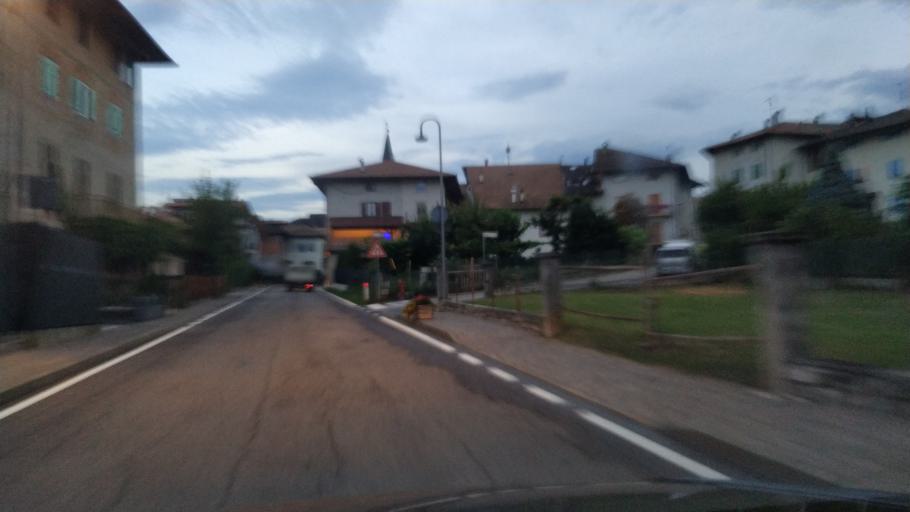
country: IT
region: Trentino-Alto Adige
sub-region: Provincia di Trento
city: Romallo
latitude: 46.3977
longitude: 11.0672
